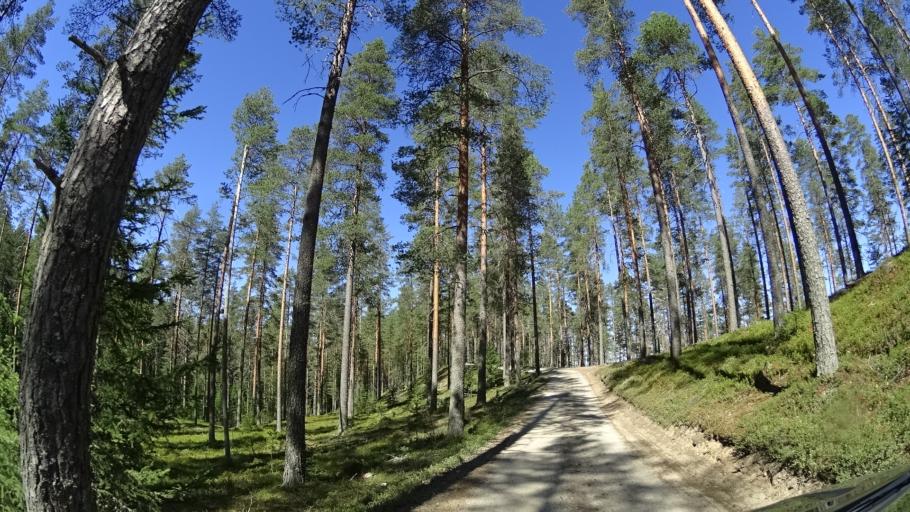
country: FI
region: Kainuu
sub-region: Kajaani
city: Vuolijoki
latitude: 63.9711
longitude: 26.8030
